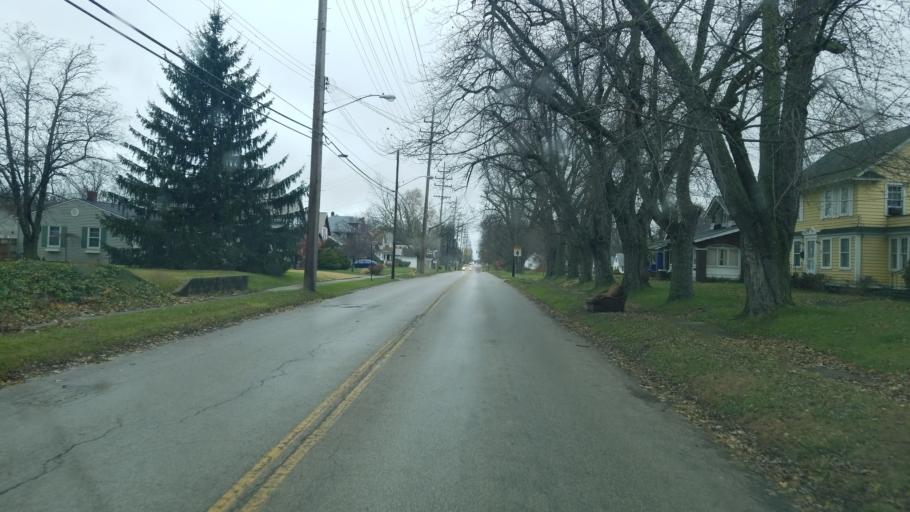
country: US
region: Ohio
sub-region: Ashtabula County
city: Edgewood
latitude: 41.8663
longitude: -80.7725
